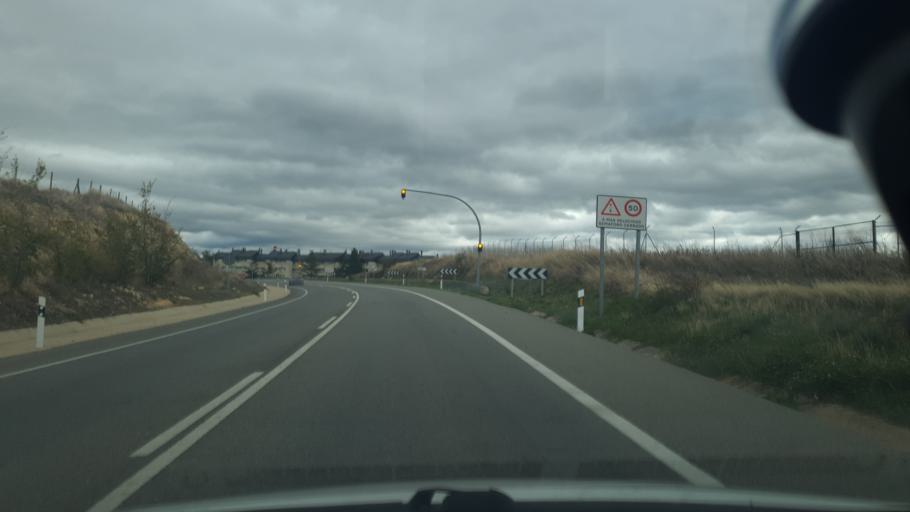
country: ES
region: Castille and Leon
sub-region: Provincia de Segovia
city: Segovia
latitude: 40.9430
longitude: -4.1399
